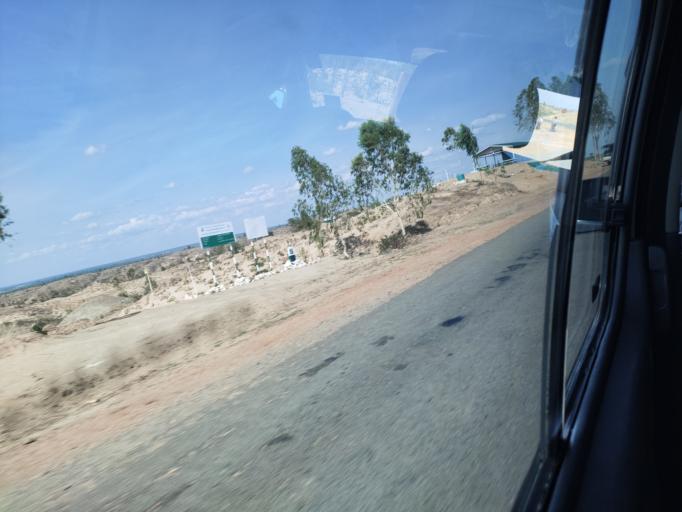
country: MM
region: Magway
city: Yenangyaung
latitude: 20.4710
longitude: 94.9209
